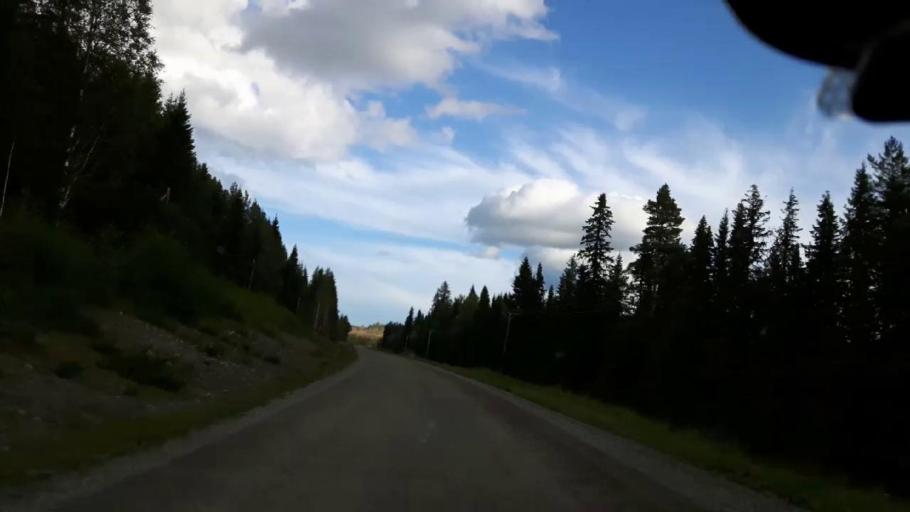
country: SE
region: Jaemtland
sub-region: Stroemsunds Kommun
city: Stroemsund
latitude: 63.3004
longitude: 15.5807
